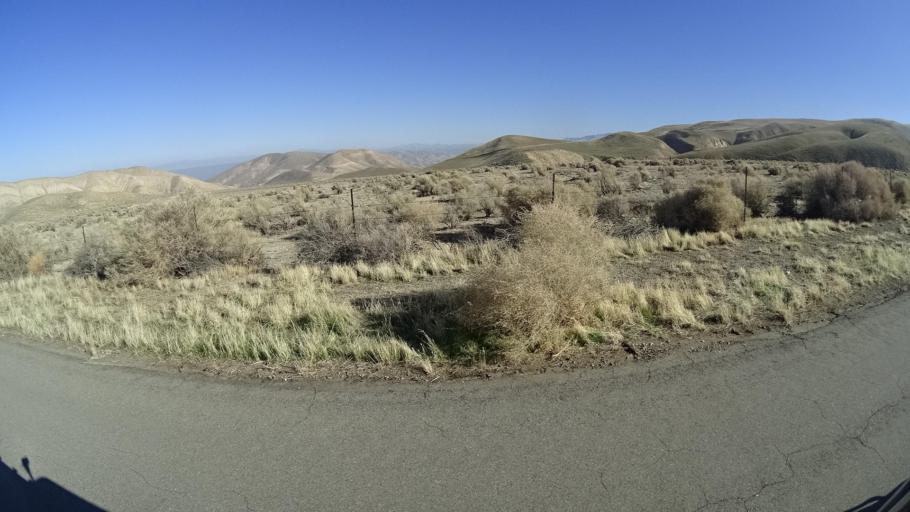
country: US
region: California
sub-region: Kern County
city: Maricopa
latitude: 34.9872
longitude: -119.3939
